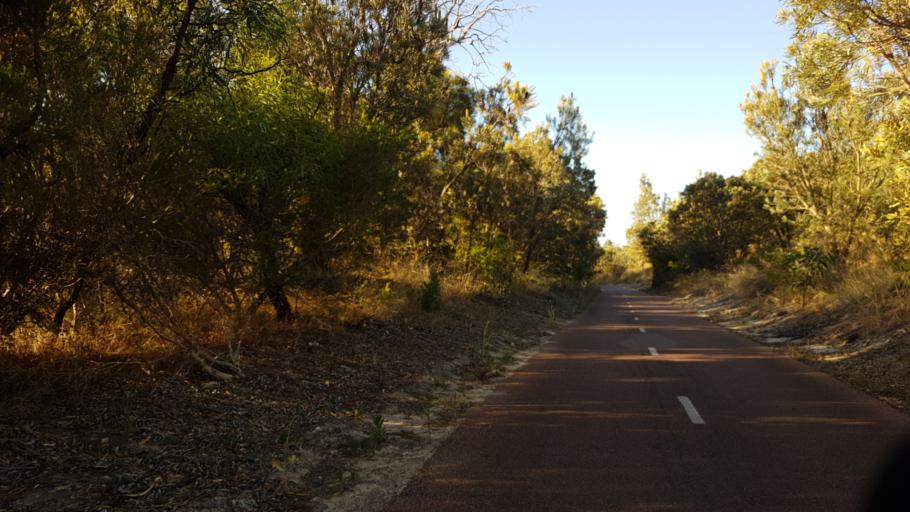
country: AU
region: Western Australia
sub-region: Kwinana
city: Bertram
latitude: -32.2307
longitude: 115.8489
